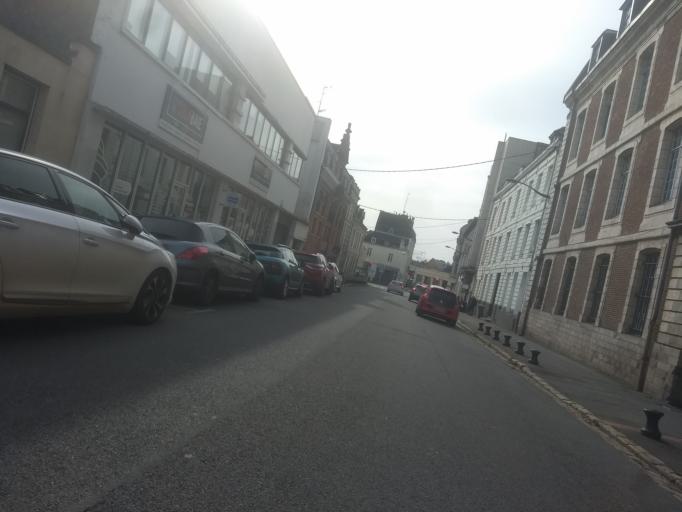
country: FR
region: Nord-Pas-de-Calais
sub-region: Departement du Pas-de-Calais
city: Arras
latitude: 50.2938
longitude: 2.7687
